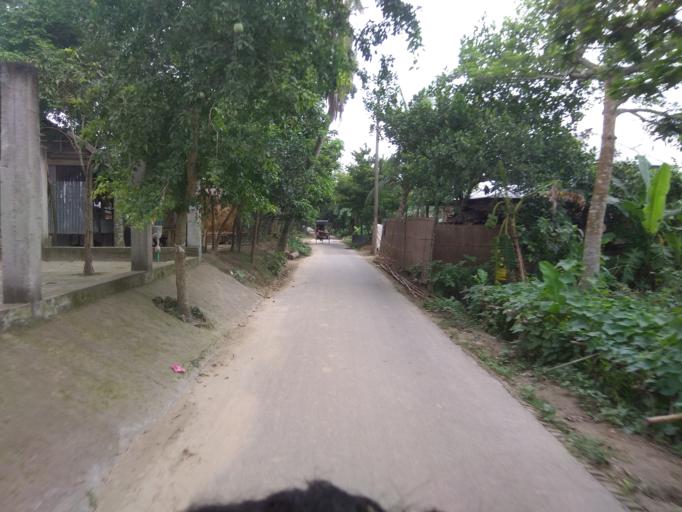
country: BD
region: Dhaka
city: Dohar
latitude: 23.4841
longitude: 90.0022
